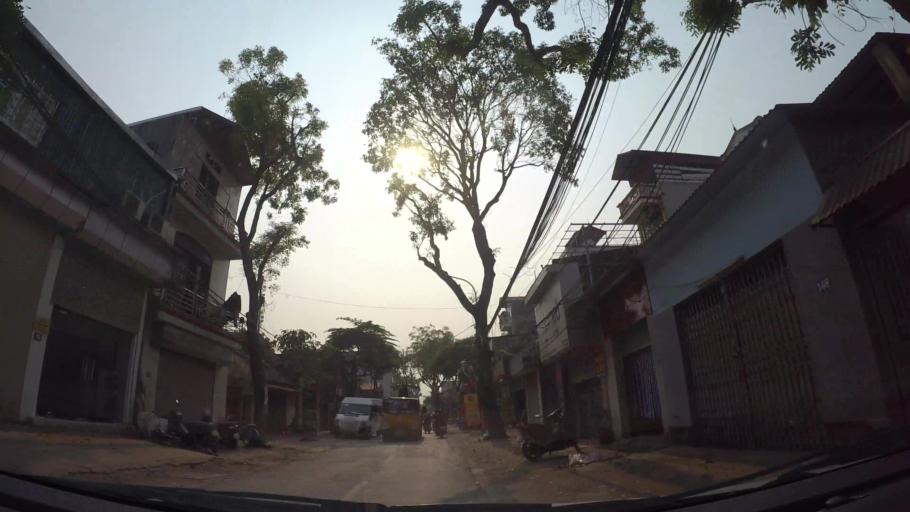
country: VN
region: Ha Noi
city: Ha Dong
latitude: 20.9958
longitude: 105.7482
